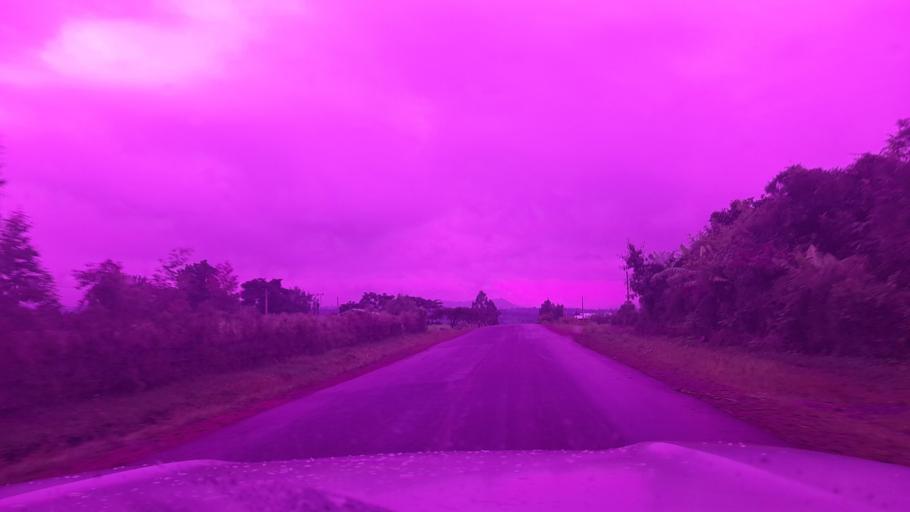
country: ET
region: Oromiya
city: Jima
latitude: 7.7905
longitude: 37.3411
